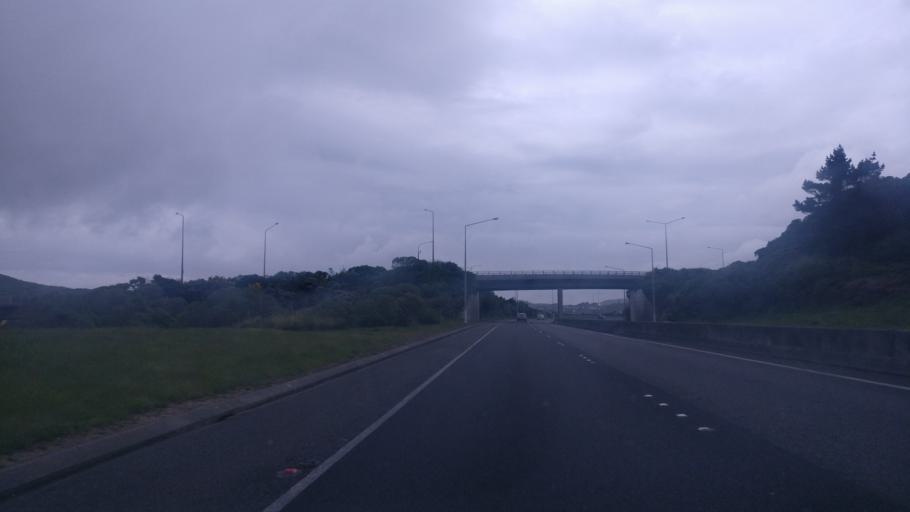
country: NZ
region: Wellington
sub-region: Porirua City
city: Porirua
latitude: -41.1329
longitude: 174.8443
